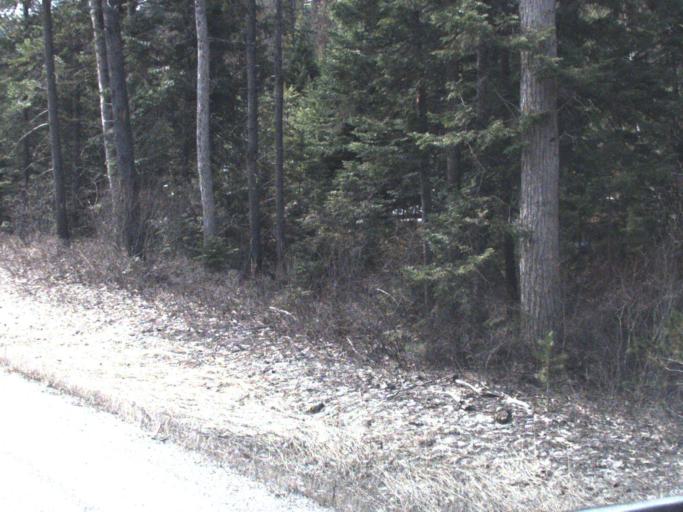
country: US
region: Washington
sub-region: Stevens County
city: Chewelah
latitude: 48.5851
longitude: -117.3519
